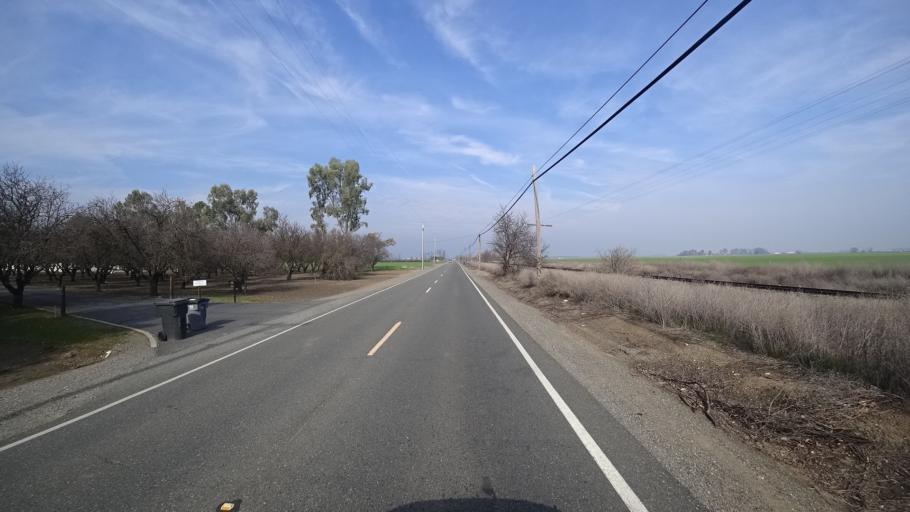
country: US
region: California
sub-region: Yolo County
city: Davis
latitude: 38.5756
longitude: -121.7479
